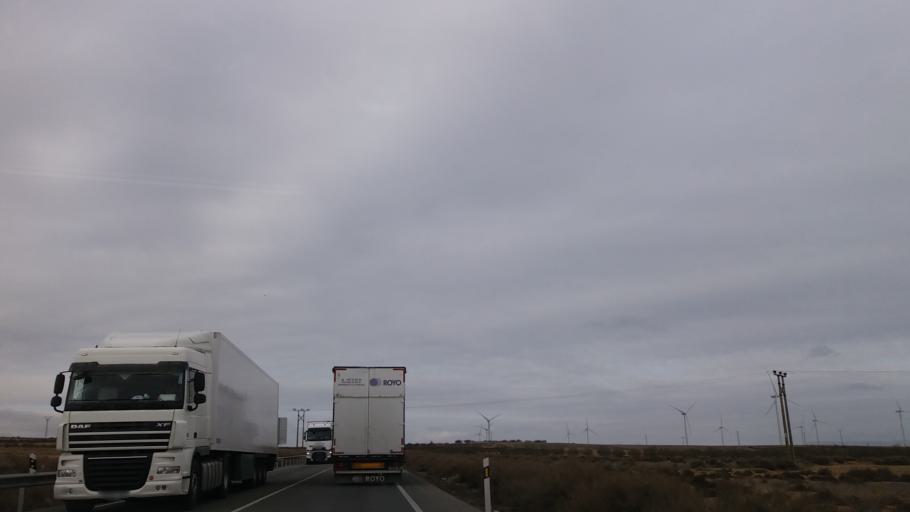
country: ES
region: Aragon
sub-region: Provincia de Zaragoza
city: Mallen
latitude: 41.8637
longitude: -1.3837
